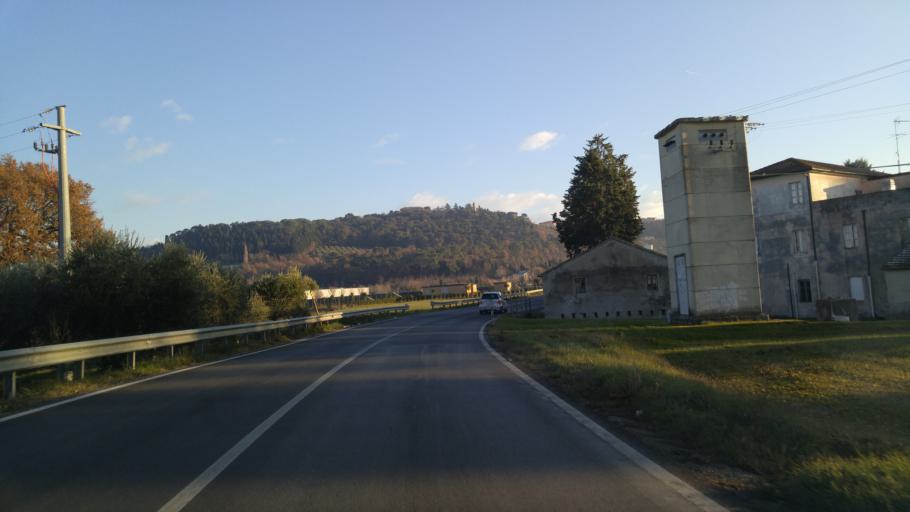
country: IT
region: The Marches
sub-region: Provincia di Ancona
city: Monterado
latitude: 43.7047
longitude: 13.0832
